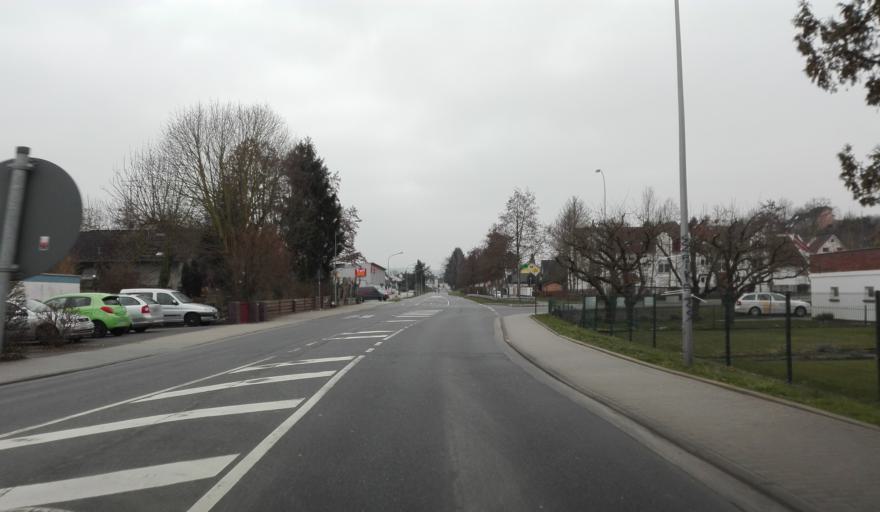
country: DE
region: Hesse
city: Ober-Ramstadt
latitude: 49.7953
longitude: 8.7388
